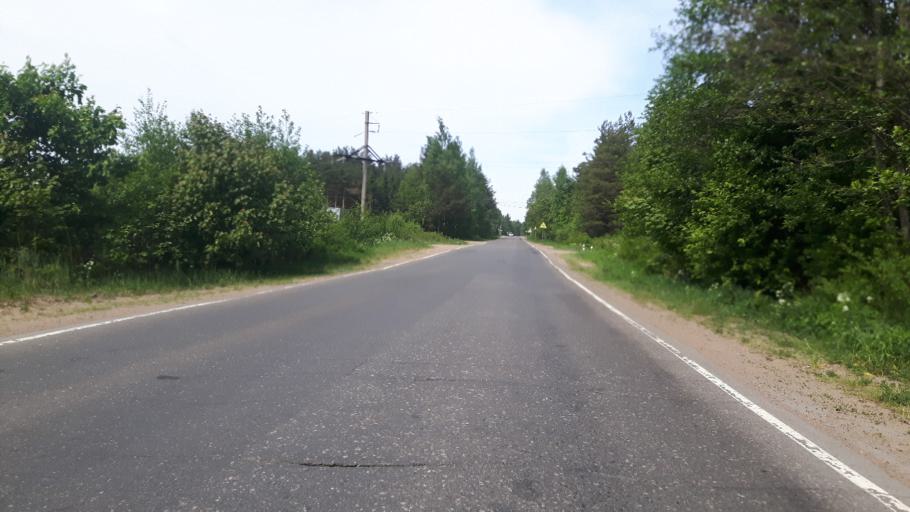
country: RU
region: Leningrad
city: Ust'-Luga
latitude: 59.6431
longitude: 28.2727
